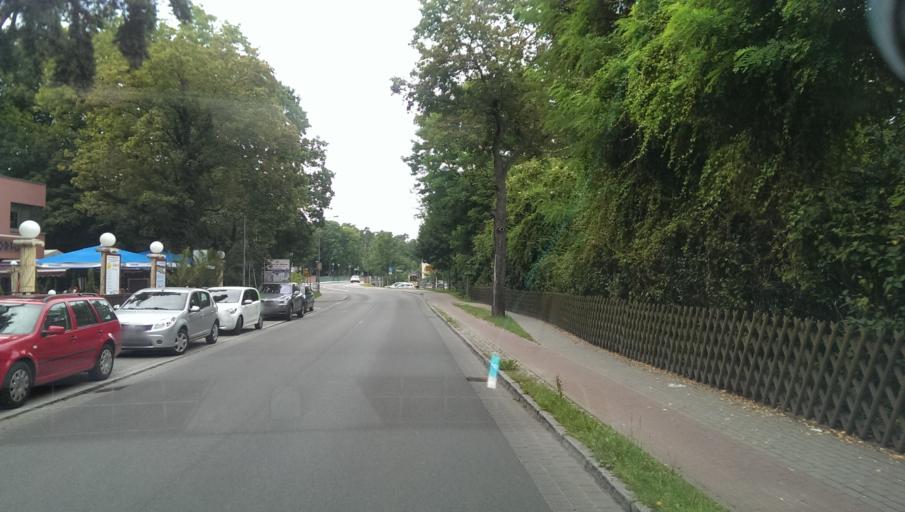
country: DE
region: Brandenburg
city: Stahnsdorf
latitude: 52.3942
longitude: 13.2088
